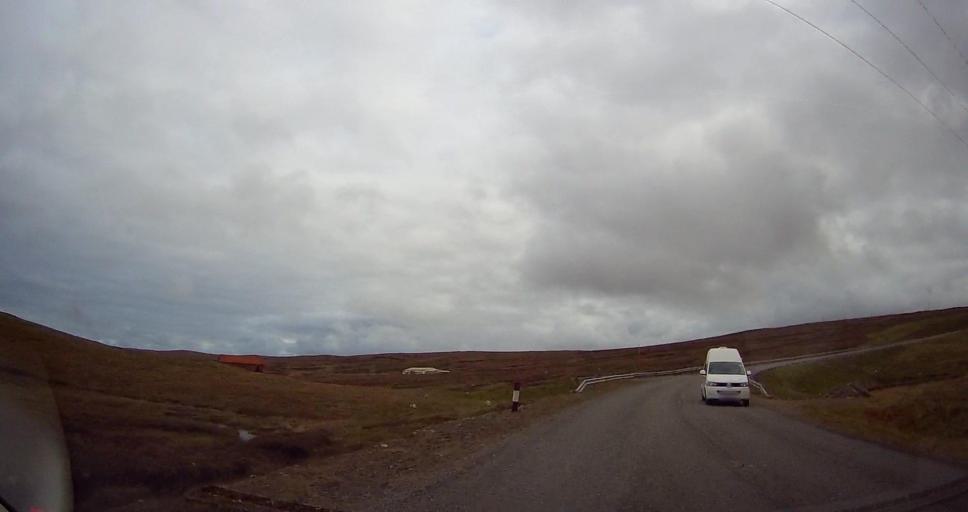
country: GB
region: Scotland
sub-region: Shetland Islands
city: Shetland
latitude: 60.6683
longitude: -1.0685
